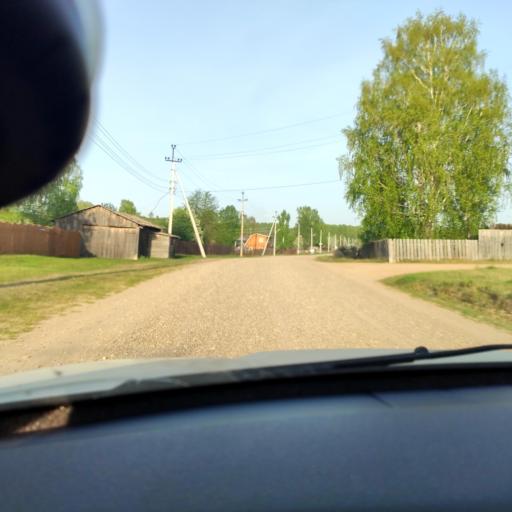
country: RU
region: Perm
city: Chermoz
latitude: 58.5999
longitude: 56.1034
